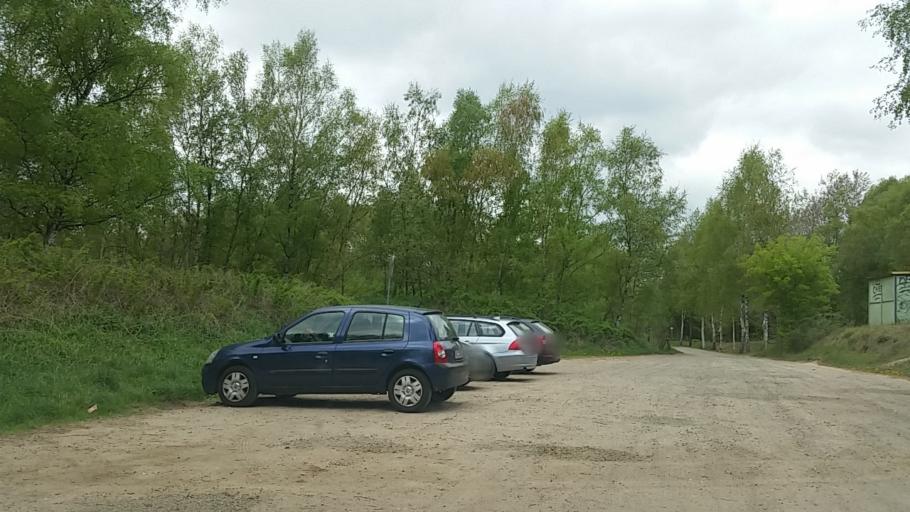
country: DE
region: Lower Saxony
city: Stelle
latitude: 53.3972
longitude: 10.0599
